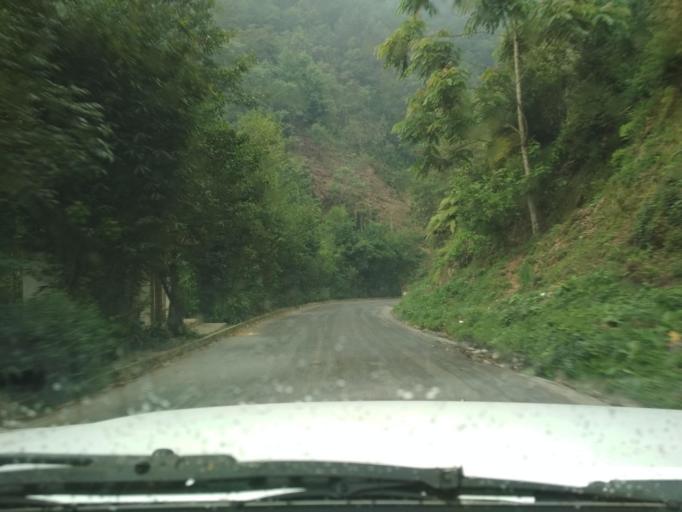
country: MX
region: Veracruz
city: La Perla
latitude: 18.9384
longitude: -97.1492
